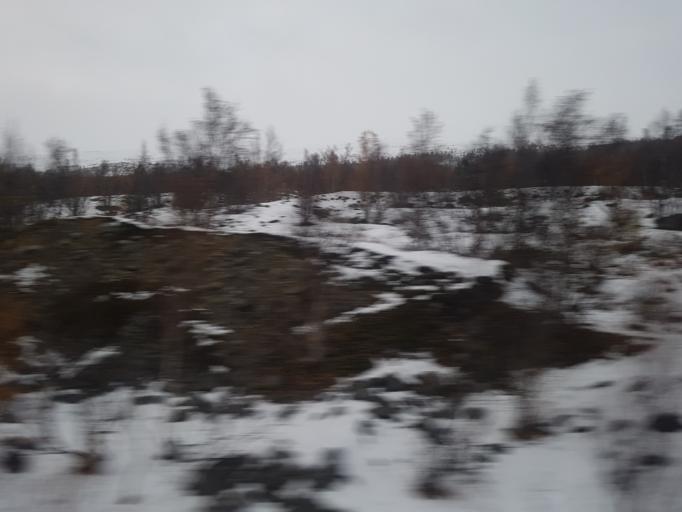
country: NO
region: Oppland
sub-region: Dovre
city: Dovre
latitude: 62.1612
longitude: 9.3758
